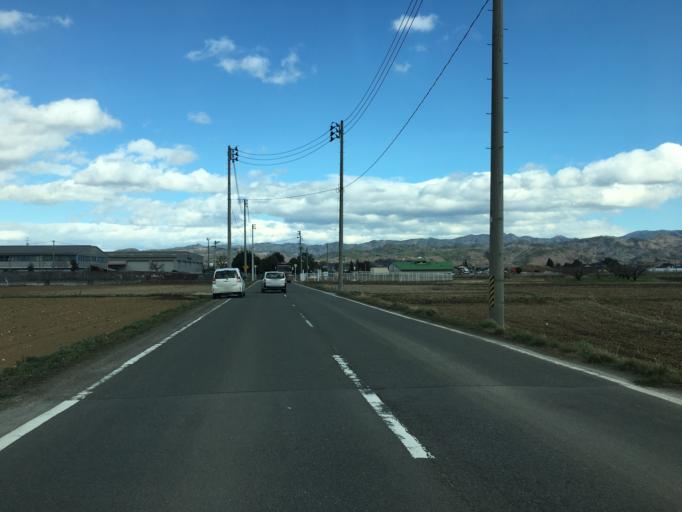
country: JP
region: Fukushima
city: Yanagawamachi-saiwaicho
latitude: 37.8570
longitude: 140.5843
